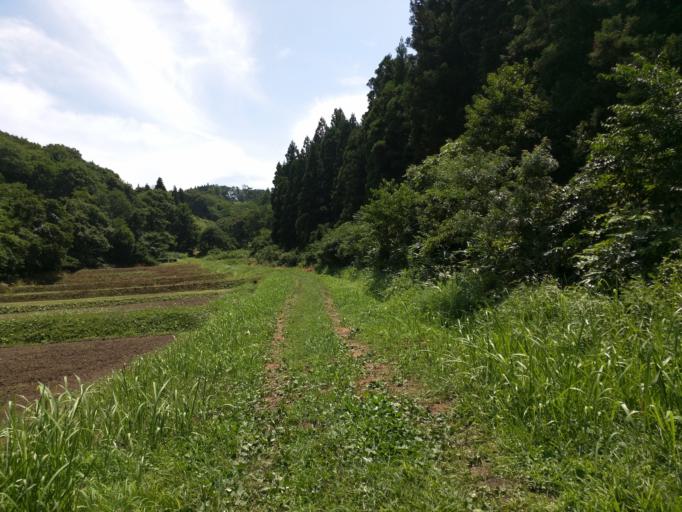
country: JP
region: Fukushima
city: Inawashiro
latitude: 37.5076
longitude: 139.9907
